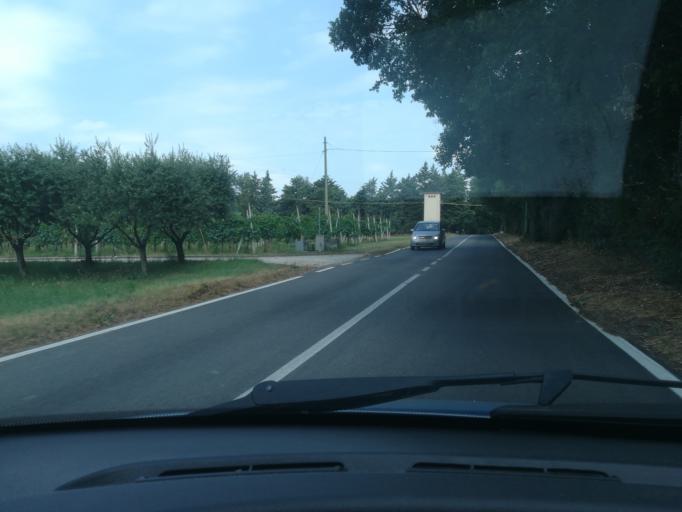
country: IT
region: The Marches
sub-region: Provincia di Macerata
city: Sforzacosta
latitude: 43.2695
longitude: 13.4375
